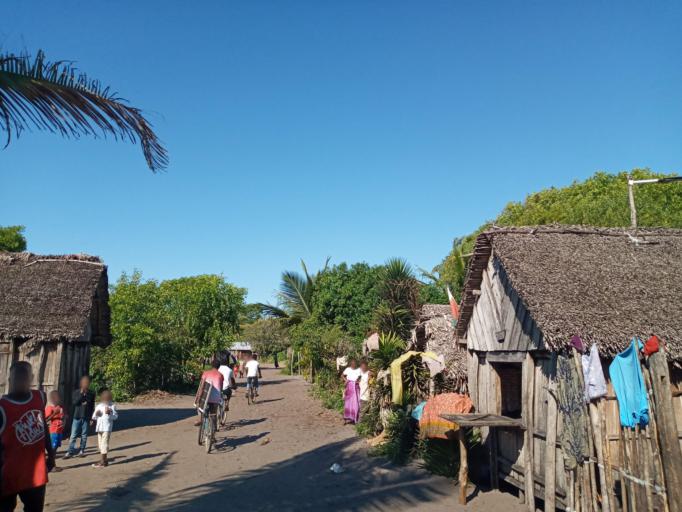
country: MG
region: Anosy
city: Fort Dauphin
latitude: -24.9091
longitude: 47.1049
